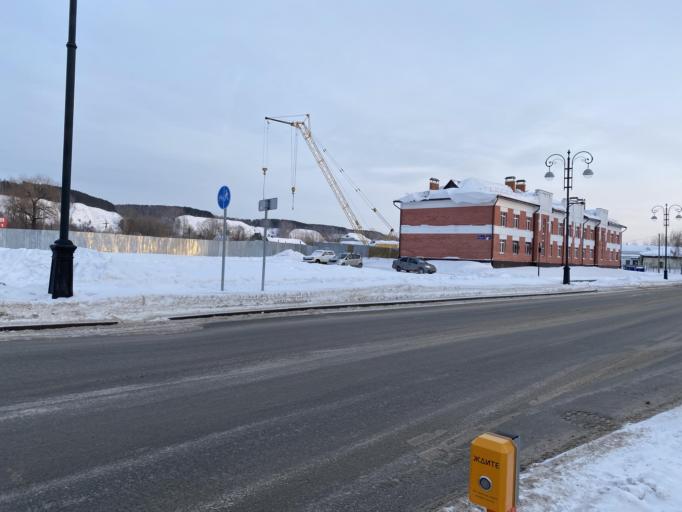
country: RU
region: Tjumen
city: Tobol'sk
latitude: 58.1931
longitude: 68.2500
